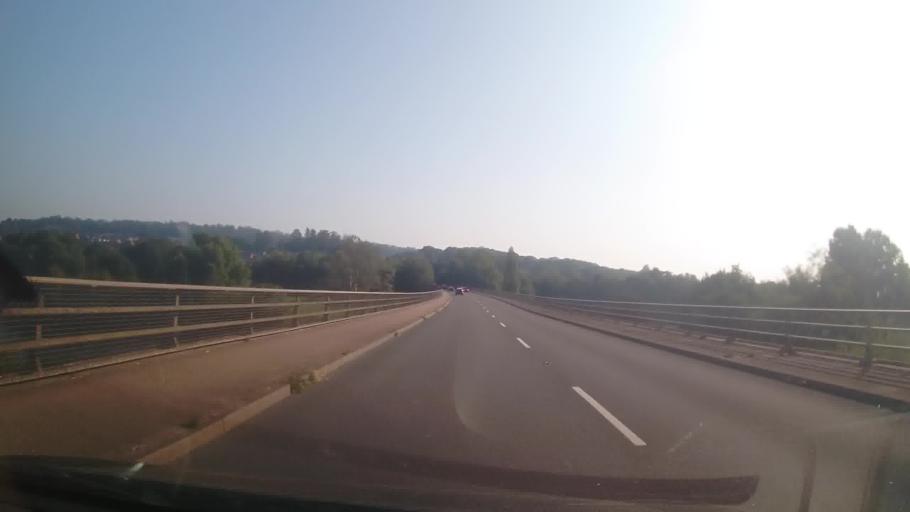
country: GB
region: England
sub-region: Shropshire
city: Bridgnorth
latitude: 52.5274
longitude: -2.4182
